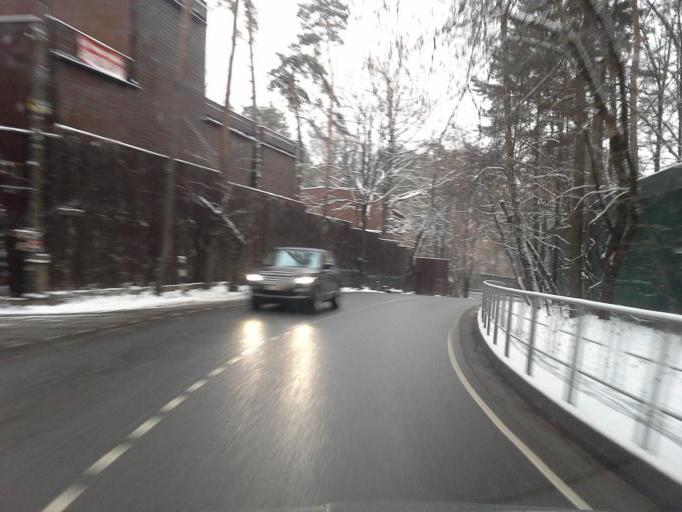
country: RU
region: Moskovskaya
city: Nikolina Gora
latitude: 55.7251
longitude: 37.0527
